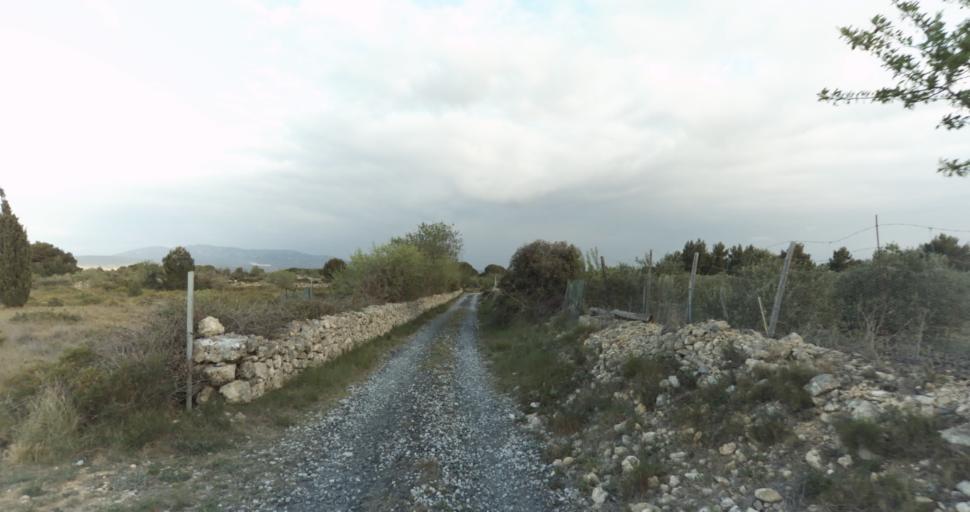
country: FR
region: Languedoc-Roussillon
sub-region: Departement de l'Aude
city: Leucate
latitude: 42.9225
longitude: 3.0201
